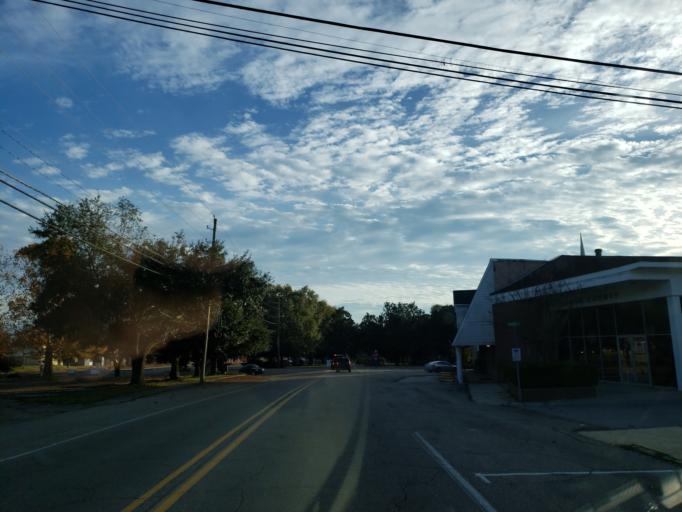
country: US
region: Mississippi
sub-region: Lamar County
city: Purvis
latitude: 31.1442
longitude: -89.4124
